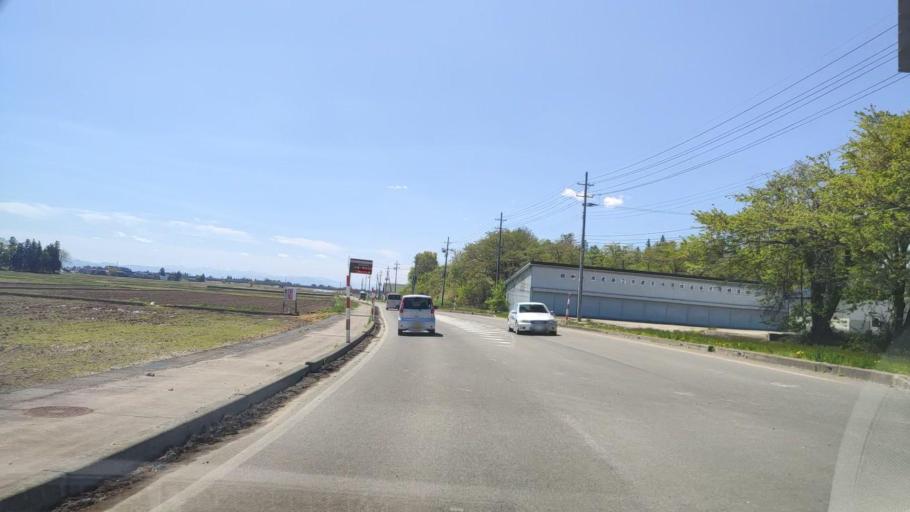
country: JP
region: Akita
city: Omagari
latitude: 39.4459
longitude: 140.4480
